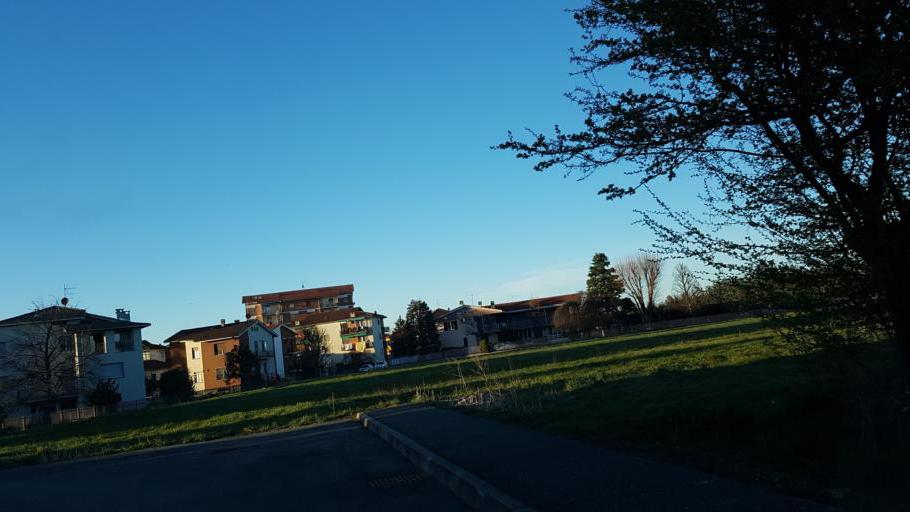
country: IT
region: Piedmont
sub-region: Provincia di Alessandria
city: Novi Ligure
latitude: 44.7604
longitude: 8.8054
